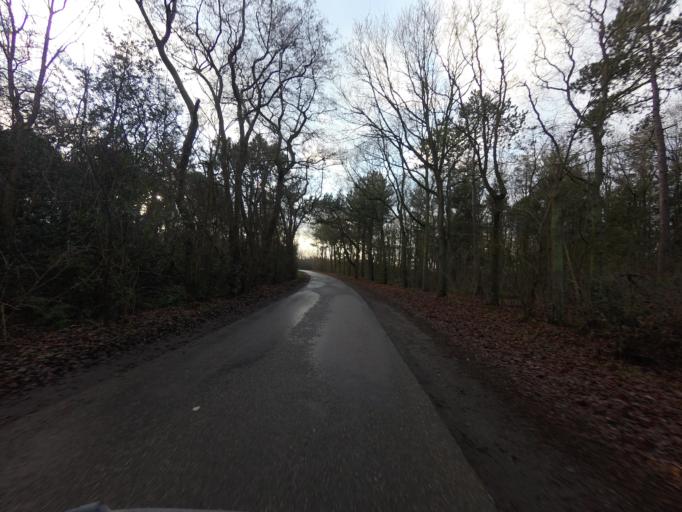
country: NL
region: North Holland
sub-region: Gemeente Texel
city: Den Burg
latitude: 53.0961
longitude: 4.7729
